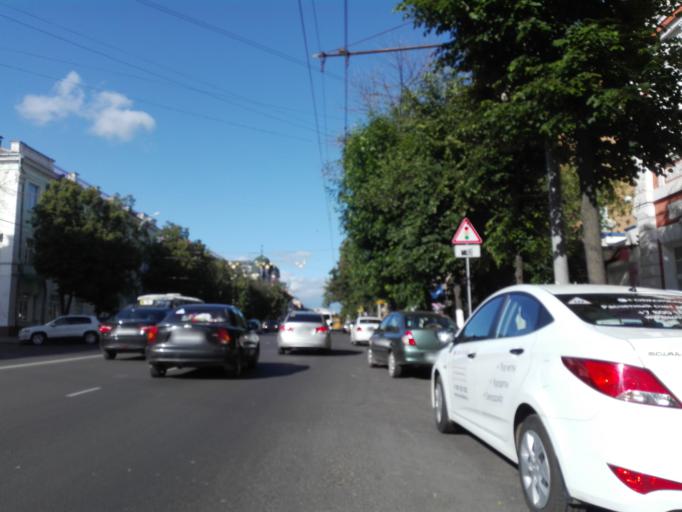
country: RU
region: Orjol
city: Orel
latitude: 52.9693
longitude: 36.0807
